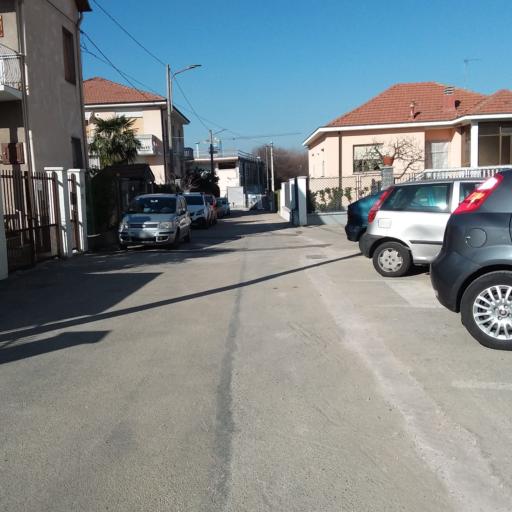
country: IT
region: Piedmont
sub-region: Provincia di Torino
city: Rivoli
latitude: 45.0722
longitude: 7.5364
